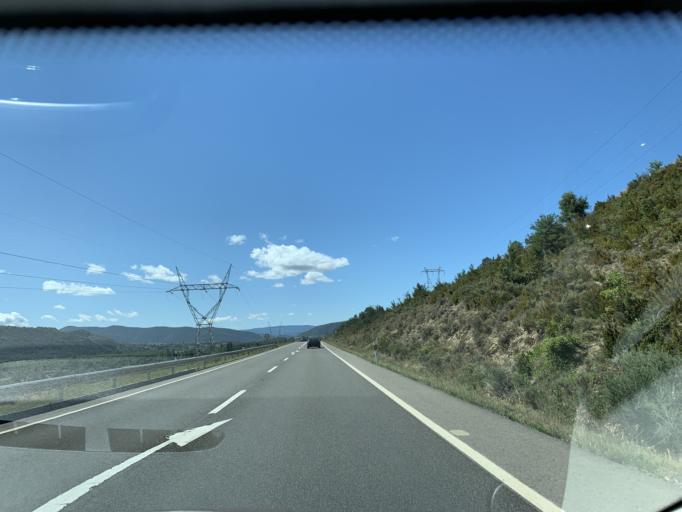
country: ES
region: Aragon
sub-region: Provincia de Huesca
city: Sabinanigo
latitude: 42.5664
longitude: -0.3277
